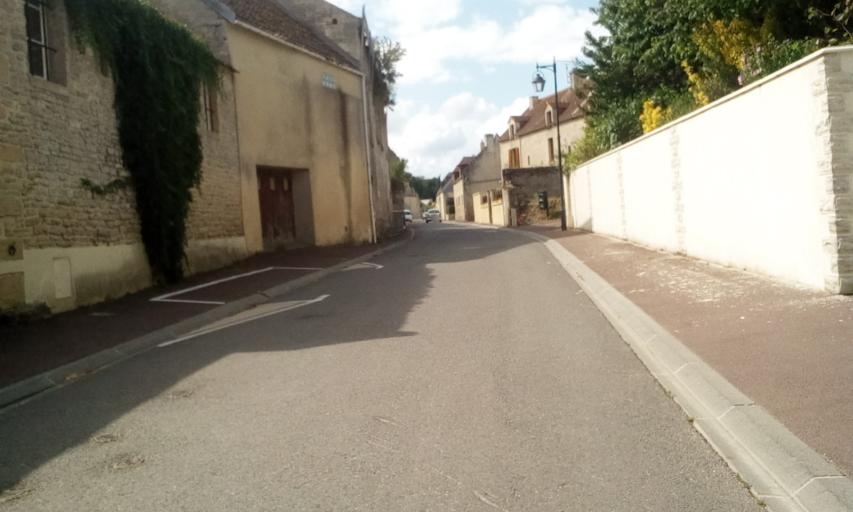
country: FR
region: Lower Normandy
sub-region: Departement du Calvados
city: Courseulles-sur-Mer
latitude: 49.3117
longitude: -0.4836
